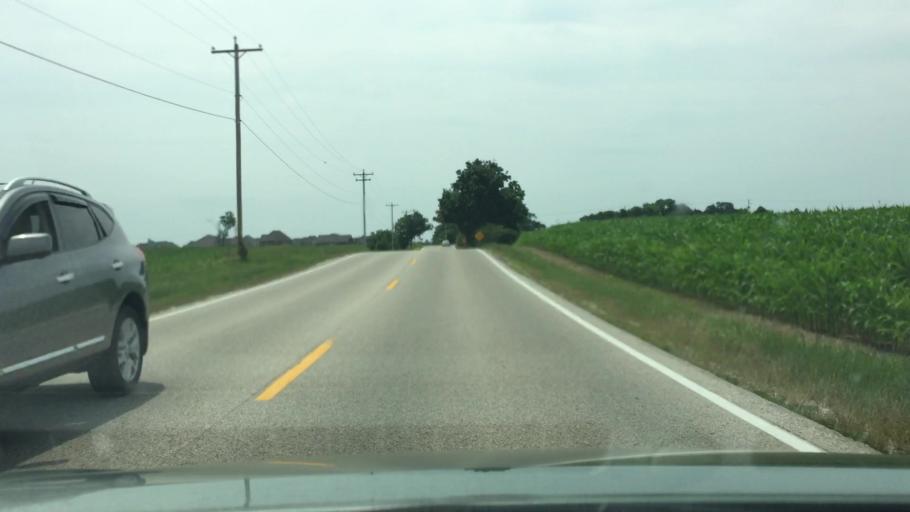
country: US
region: Wisconsin
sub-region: Waukesha County
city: Merton
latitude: 43.1229
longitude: -88.3079
